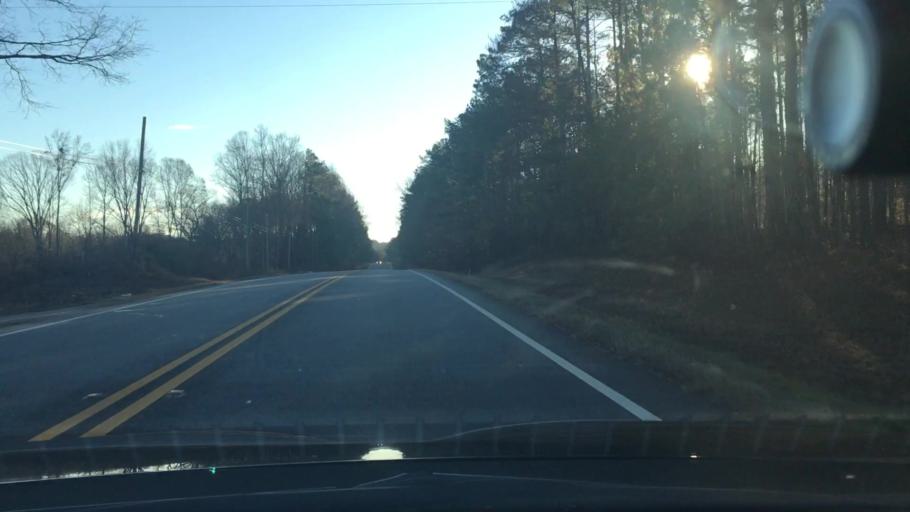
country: US
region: Georgia
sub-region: Coweta County
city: Senoia
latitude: 33.2613
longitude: -84.5127
